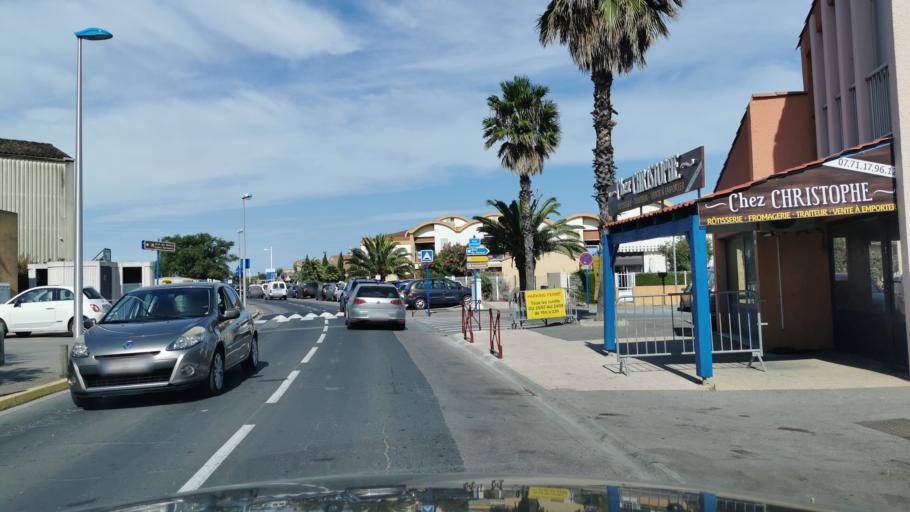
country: FR
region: Languedoc-Roussillon
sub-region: Departement de l'Aude
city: Gruissan
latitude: 43.1082
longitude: 3.0937
